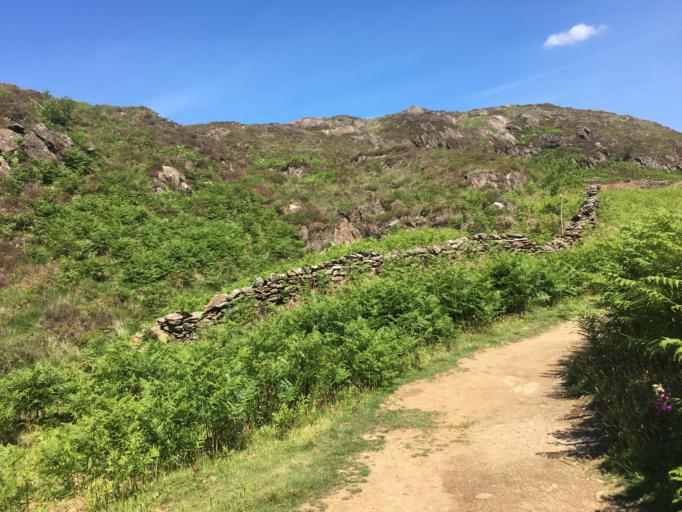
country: GB
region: Wales
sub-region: Gwynedd
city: Penrhyndeudraeth
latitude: 53.0040
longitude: -4.0838
